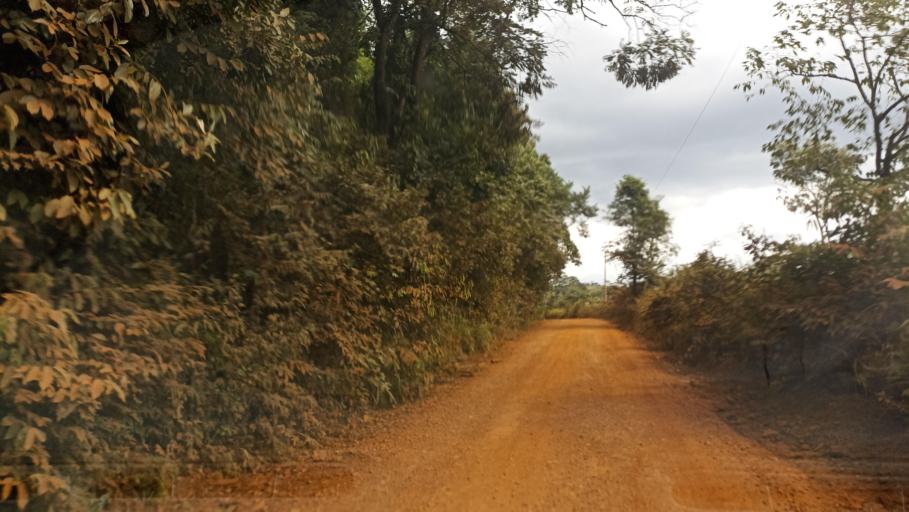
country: BR
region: Minas Gerais
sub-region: Itabirito
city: Itabirito
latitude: -20.3882
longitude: -43.7594
